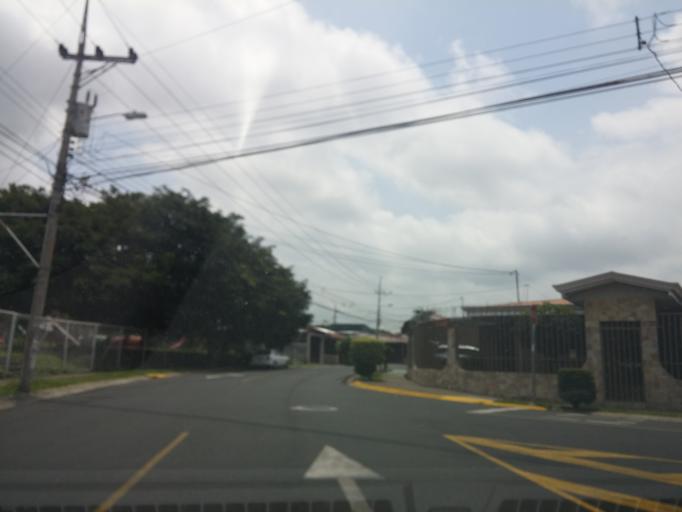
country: CR
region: Heredia
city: San Francisco
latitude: 9.9901
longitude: -84.1297
